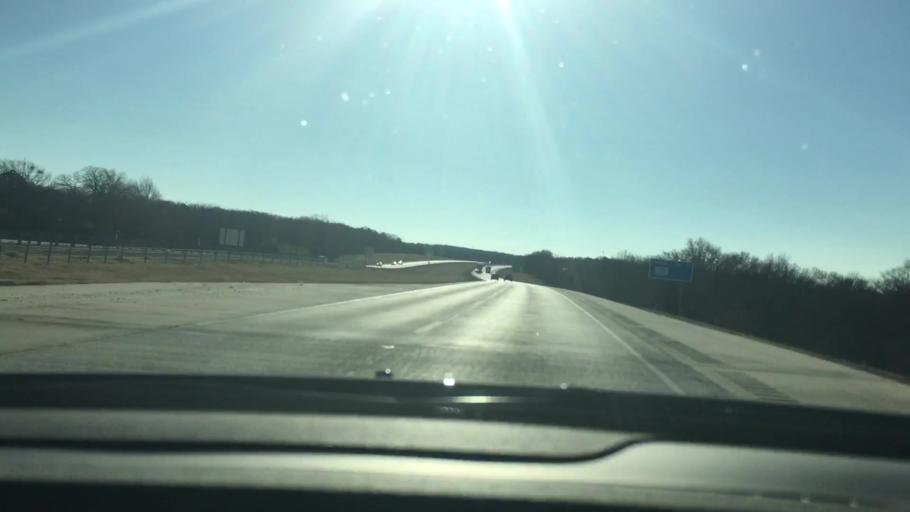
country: US
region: Oklahoma
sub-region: Carter County
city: Ardmore
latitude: 34.1582
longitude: -97.1634
